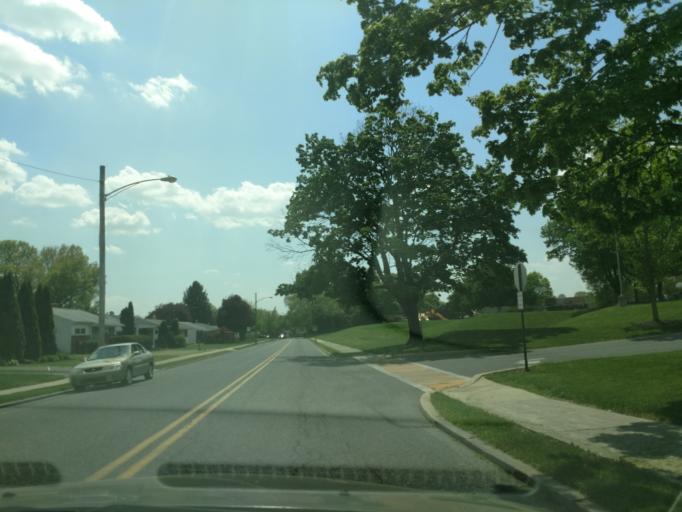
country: US
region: Pennsylvania
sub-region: Lebanon County
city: Hebron
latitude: 40.3360
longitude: -76.4030
